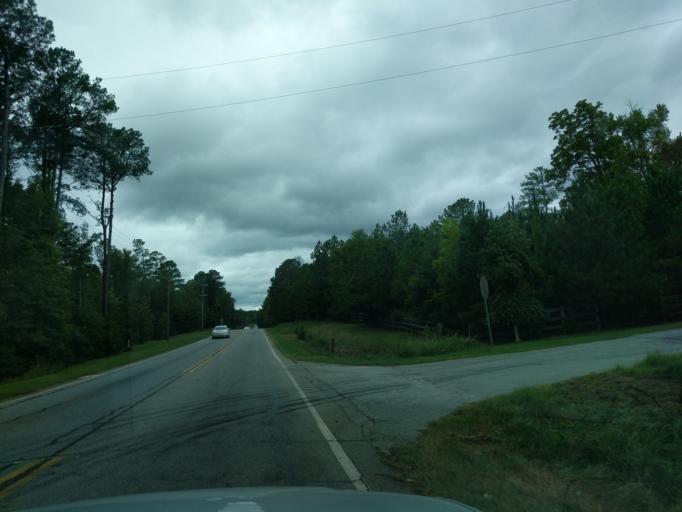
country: US
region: Georgia
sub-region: Wilkes County
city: Washington
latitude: 33.6905
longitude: -82.6670
